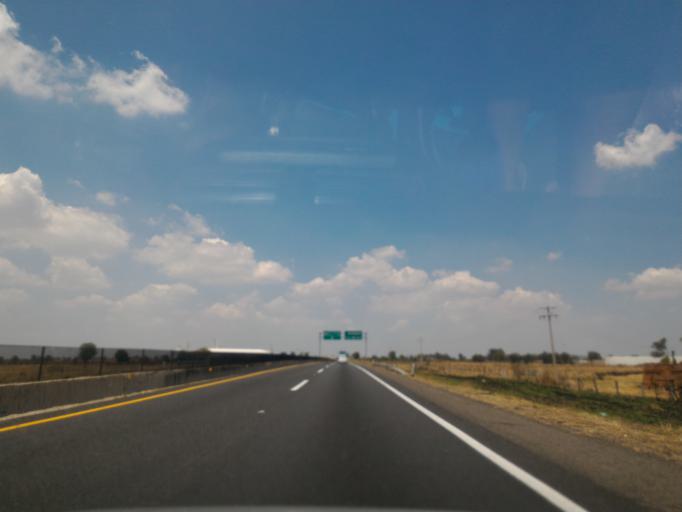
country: MX
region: Jalisco
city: Tepatitlan de Morelos
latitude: 20.8853
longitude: -102.7246
